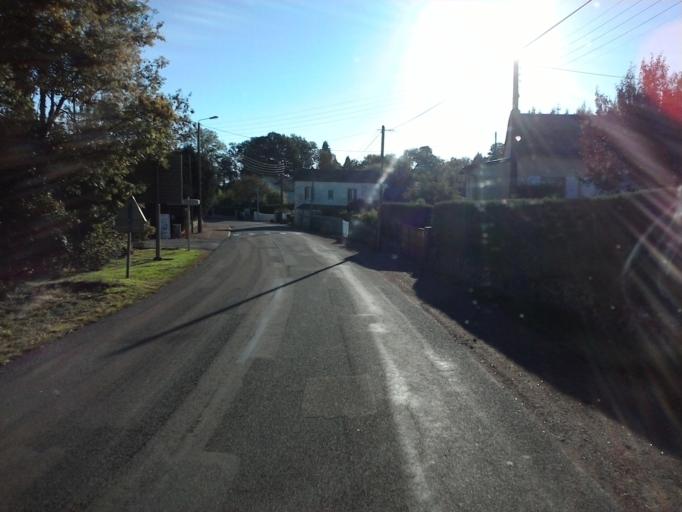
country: FR
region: Bourgogne
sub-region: Departement de la Cote-d'Or
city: Saulieu
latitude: 47.2748
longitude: 4.2258
